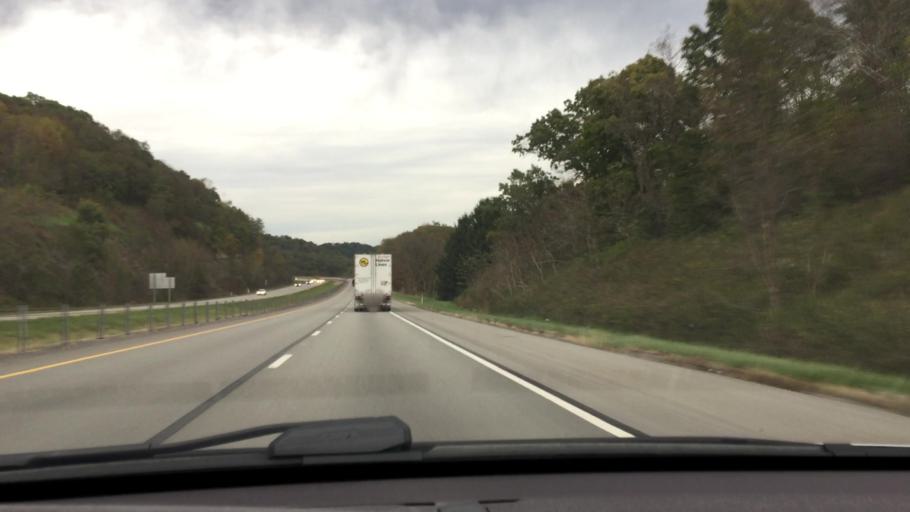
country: US
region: Pennsylvania
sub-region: Beaver County
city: Beaver Falls
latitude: 40.7166
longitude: -80.3730
